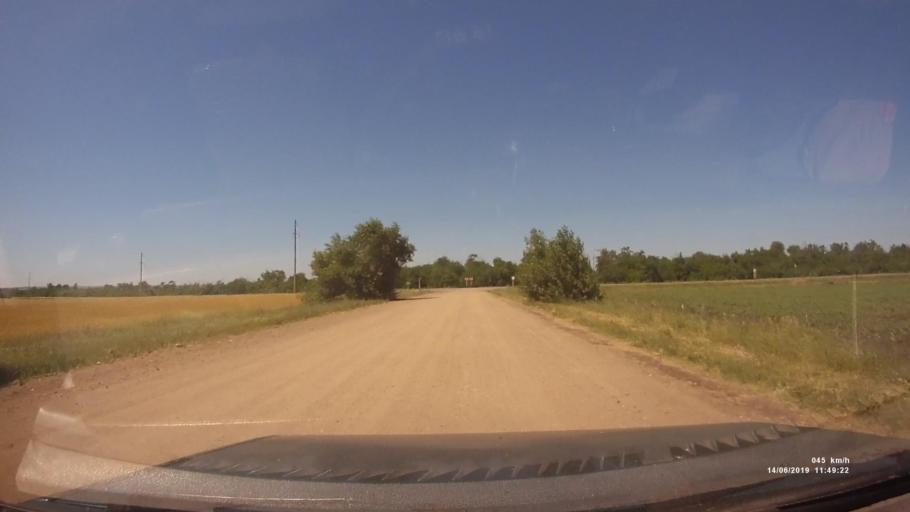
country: RU
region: Rostov
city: Kazanskaya
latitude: 49.8532
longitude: 41.2772
